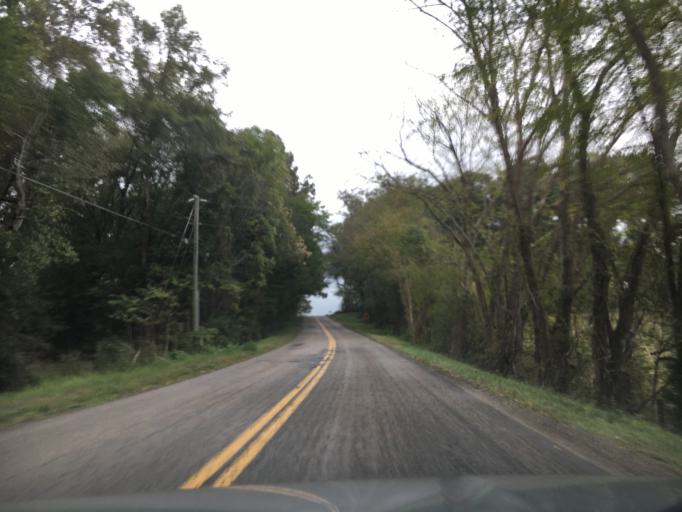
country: US
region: Virginia
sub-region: Amelia County
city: Amelia Court House
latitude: 37.3964
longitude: -77.9719
